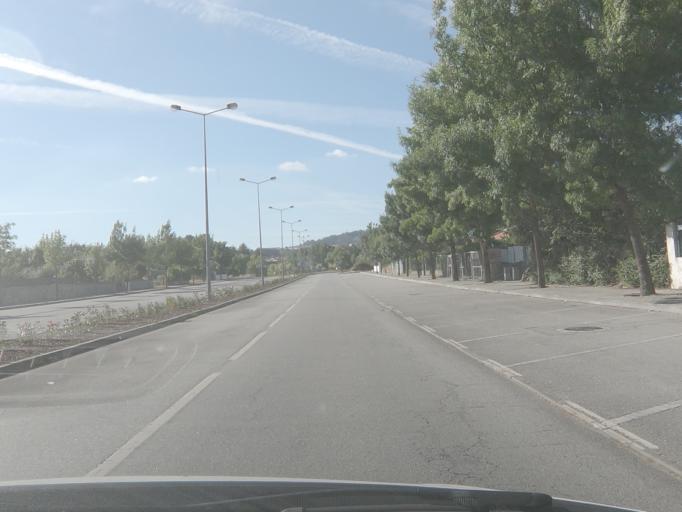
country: PT
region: Viseu
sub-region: Viseu
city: Viseu
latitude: 40.6702
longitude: -7.9043
